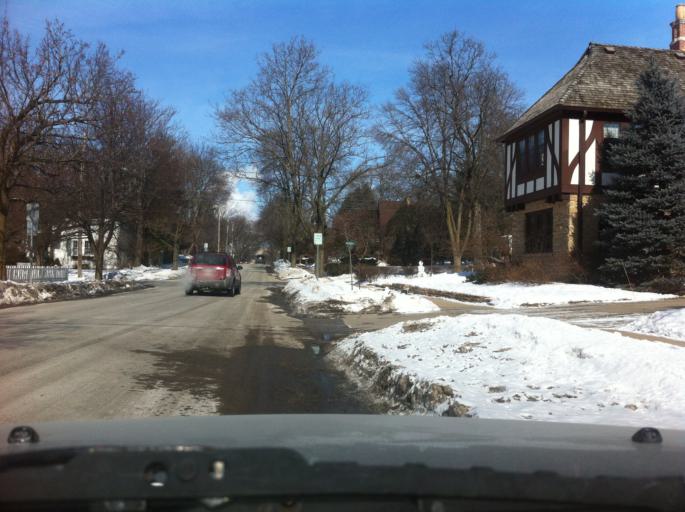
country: US
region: Wisconsin
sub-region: Dane County
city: Shorewood Hills
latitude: 43.0680
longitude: -89.4258
